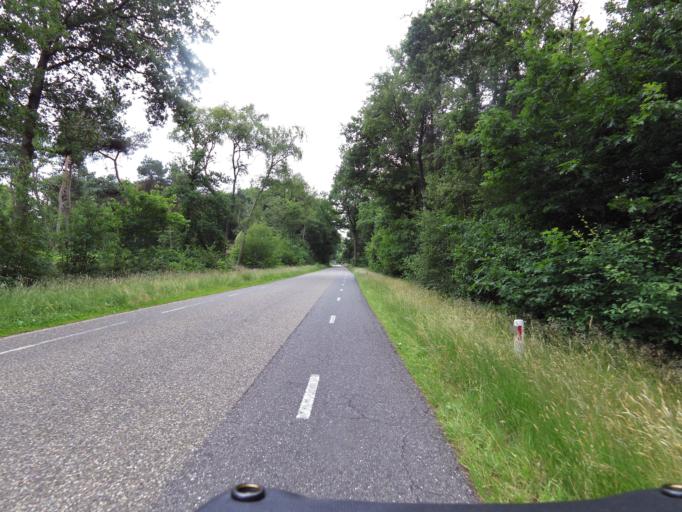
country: NL
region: North Brabant
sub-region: Gemeente Bladel en Netersel
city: Bladel
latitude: 51.4131
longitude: 5.2161
